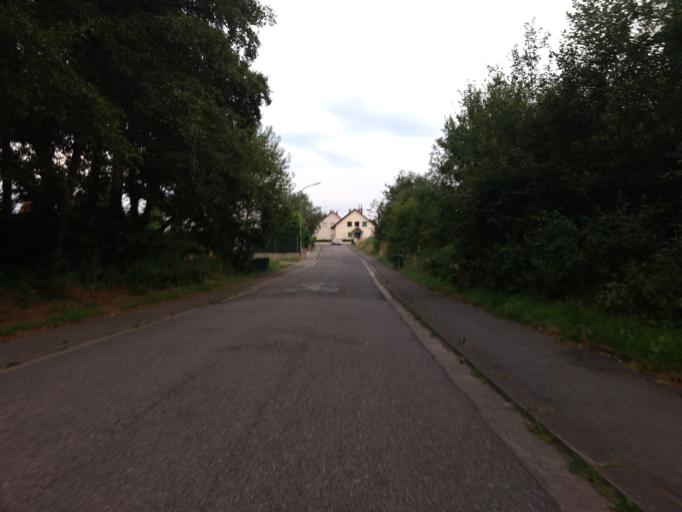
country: DE
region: Saarland
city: Wallerfangen
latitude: 49.3265
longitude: 6.7038
